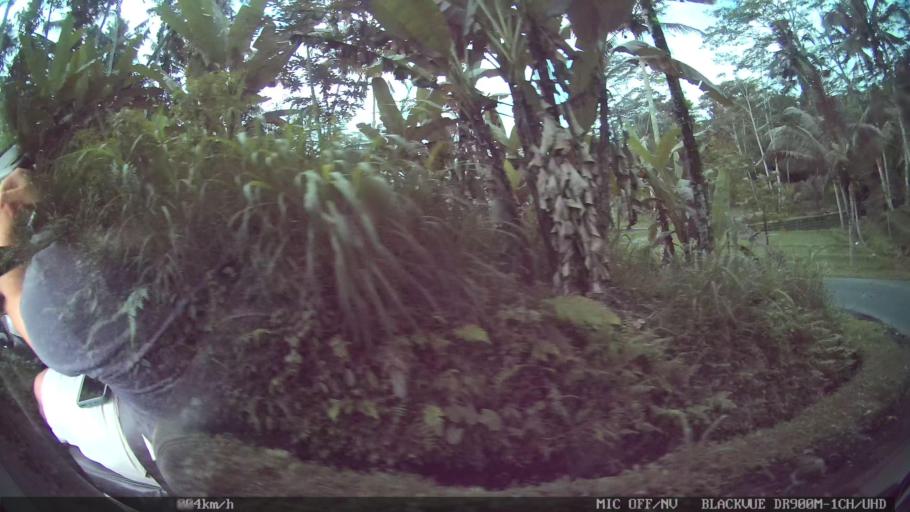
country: ID
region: Bali
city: Banjar Petak
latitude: -8.4494
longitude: 115.3258
